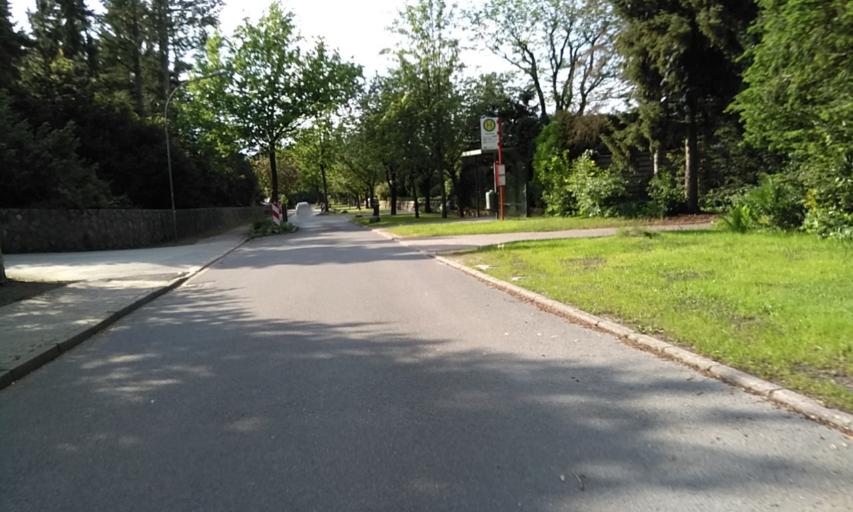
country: DE
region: Lower Saxony
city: Buxtehude
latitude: 53.4588
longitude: 9.7043
